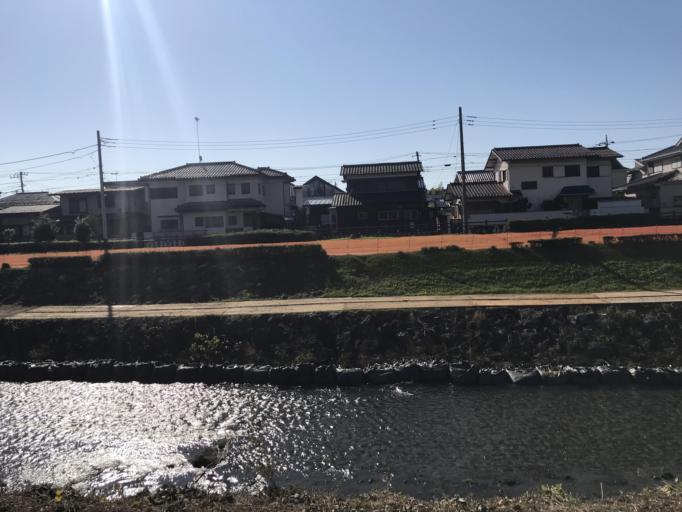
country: JP
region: Saitama
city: Tokorozawa
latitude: 35.7884
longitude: 139.5185
